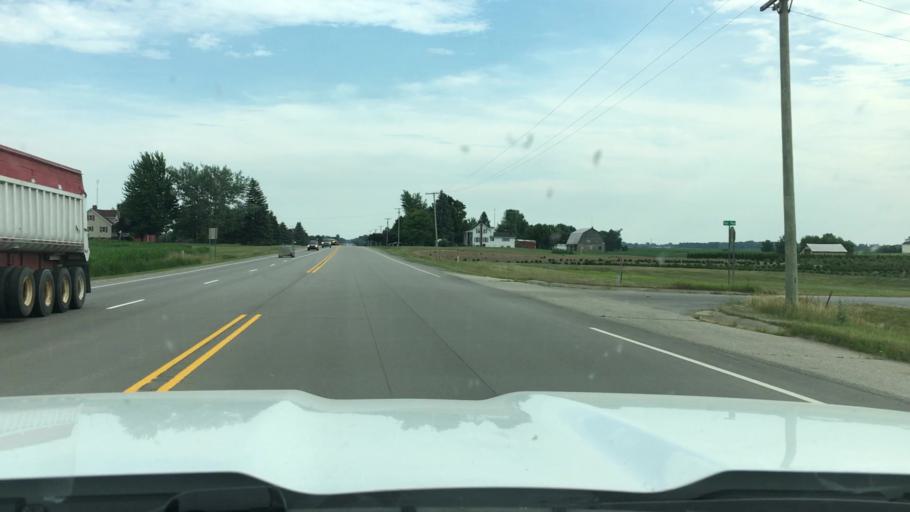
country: US
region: Michigan
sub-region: Sanilac County
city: Marlette
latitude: 43.3771
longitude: -83.0858
